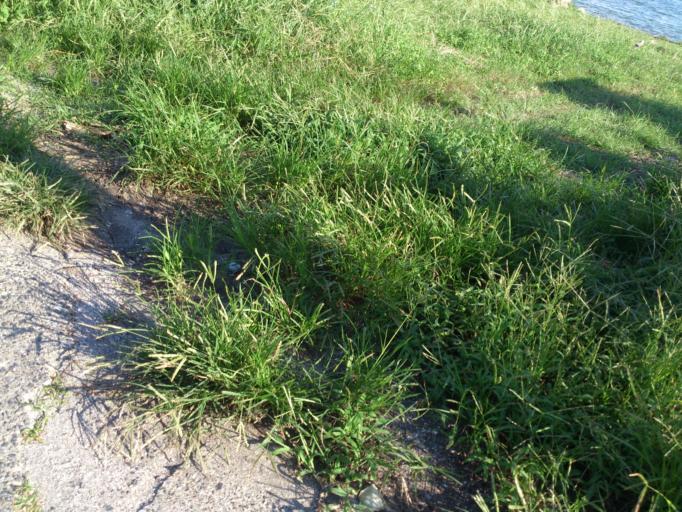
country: JP
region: Chiba
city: Tateyama
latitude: 35.0526
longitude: 139.8300
